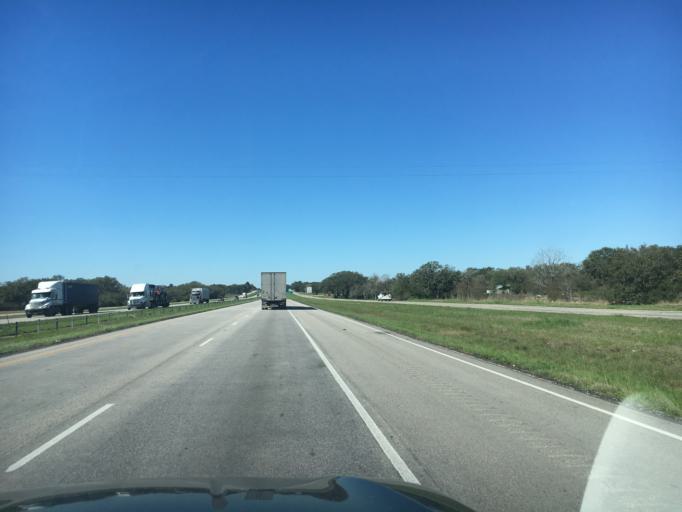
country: US
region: Texas
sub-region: Colorado County
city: Columbus
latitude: 29.7226
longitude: -96.4245
